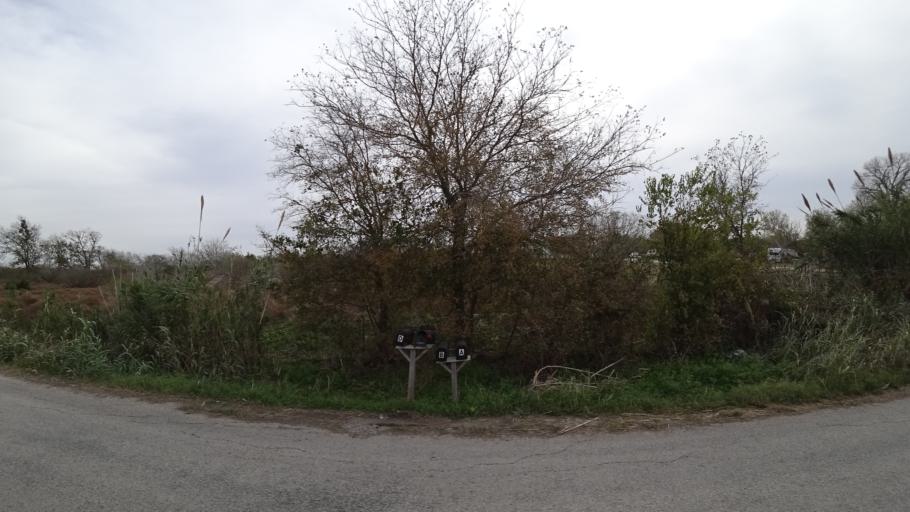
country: US
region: Texas
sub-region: Travis County
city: Garfield
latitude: 30.1119
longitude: -97.5830
